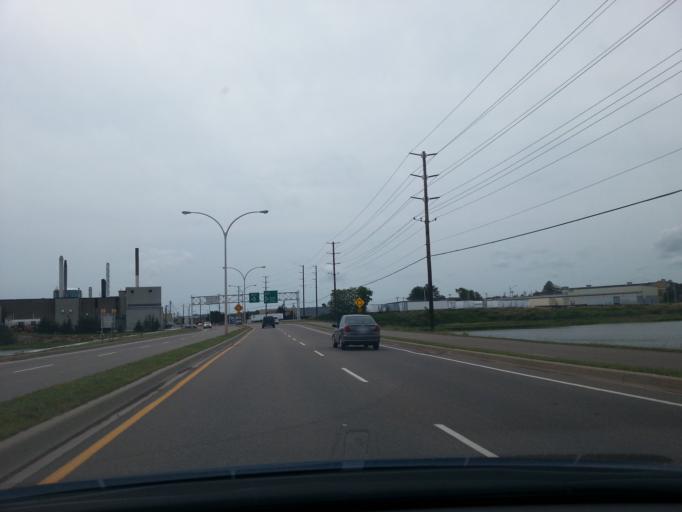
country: CA
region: Prince Edward Island
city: Charlottetown
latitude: 46.2533
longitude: -63.1060
